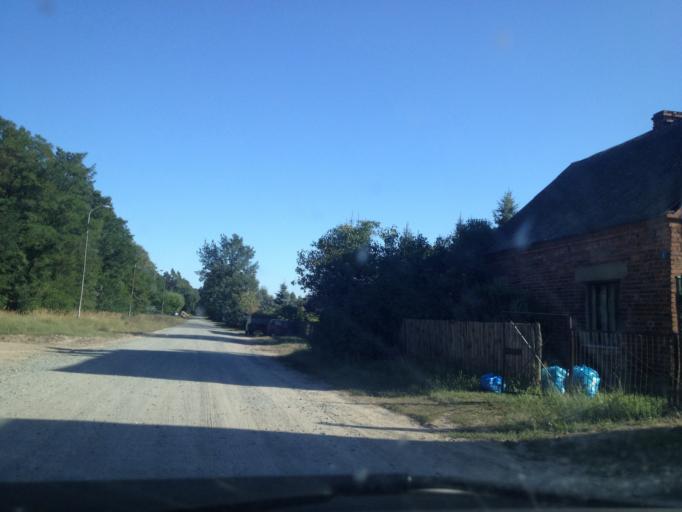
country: PL
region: Greater Poland Voivodeship
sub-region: Powiat sredzki
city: Zaniemysl
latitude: 52.1126
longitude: 17.1177
